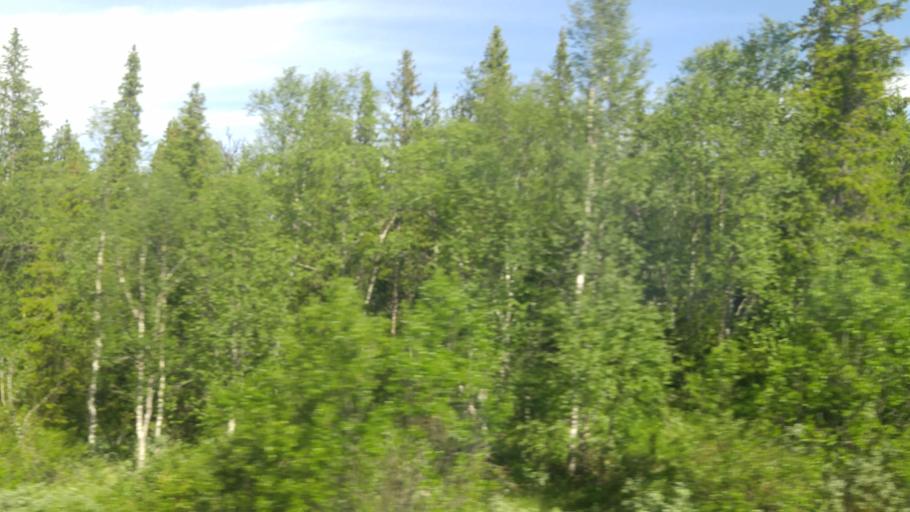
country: SE
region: Jaemtland
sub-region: Are Kommun
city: Are
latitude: 63.3151
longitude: 12.4981
